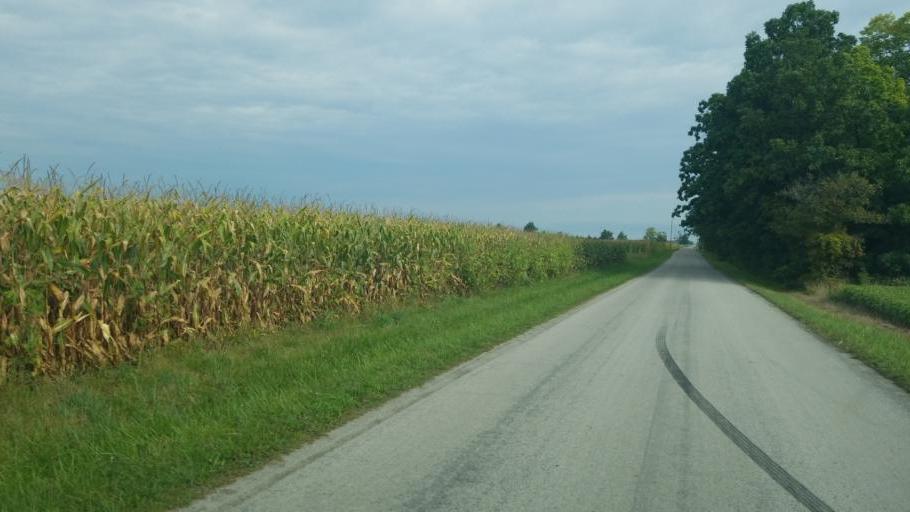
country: US
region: Ohio
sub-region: Marion County
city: Marion
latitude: 40.7260
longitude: -83.1307
